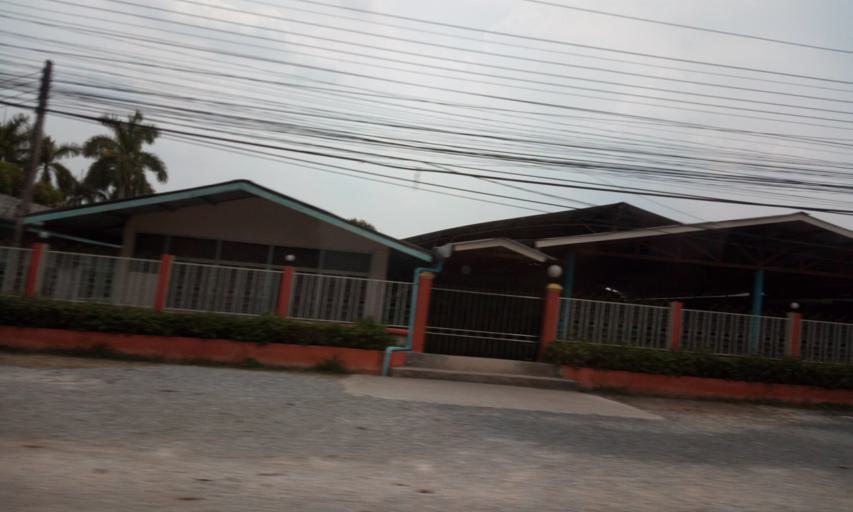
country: TH
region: Phayao
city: Chiang Kham
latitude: 19.5361
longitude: 100.2998
